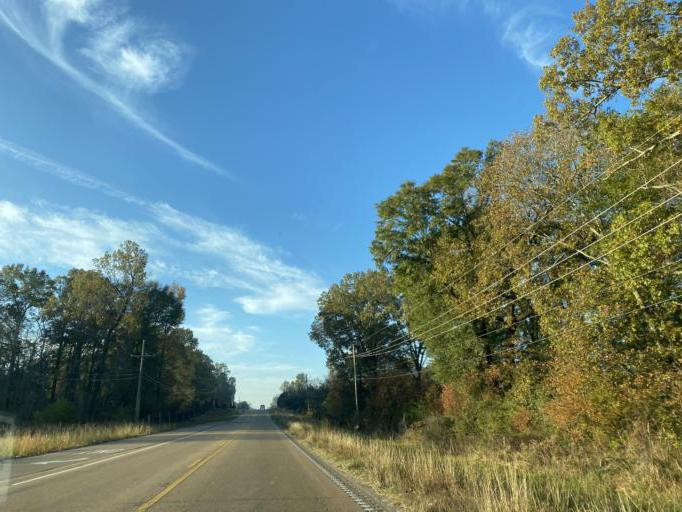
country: US
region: Mississippi
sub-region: Madison County
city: Madison
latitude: 32.5094
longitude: -90.0867
